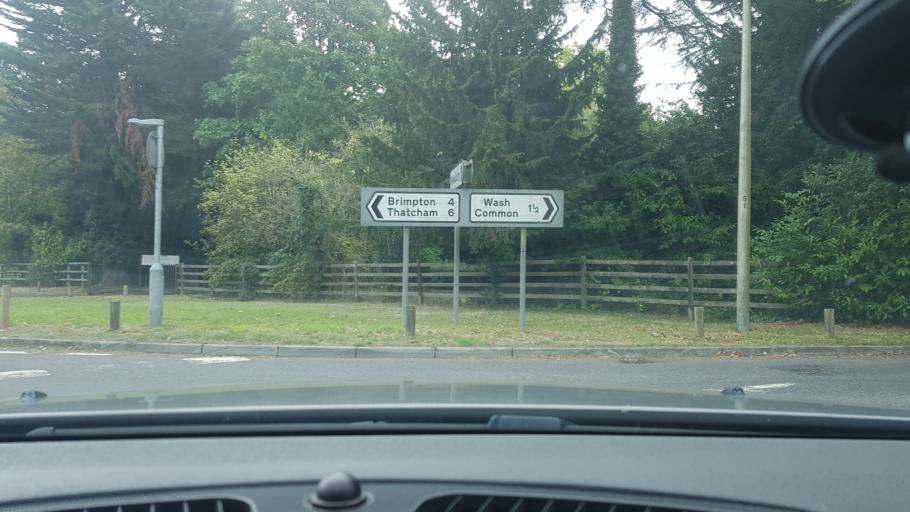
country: GB
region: England
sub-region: West Berkshire
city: Greenham
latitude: 51.3848
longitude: -1.3069
